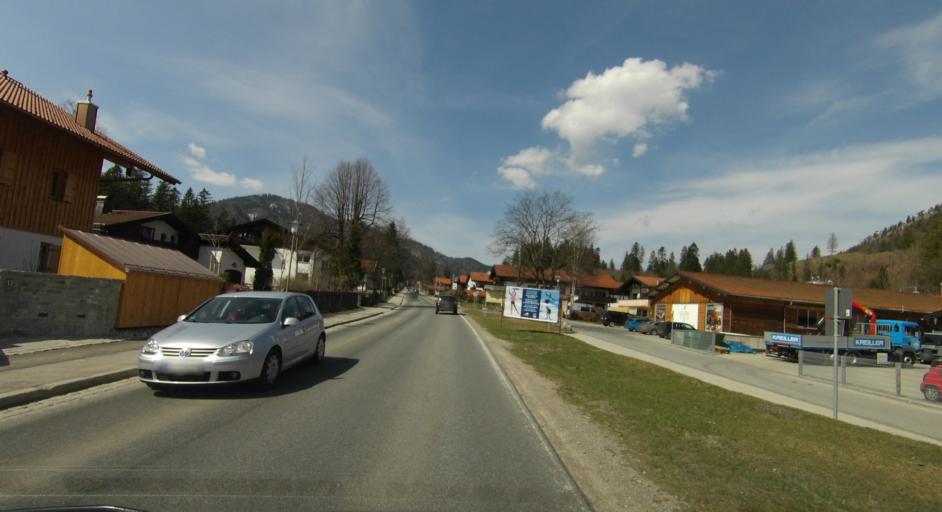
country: DE
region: Bavaria
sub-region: Upper Bavaria
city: Schliersee
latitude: 47.7022
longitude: 11.8858
